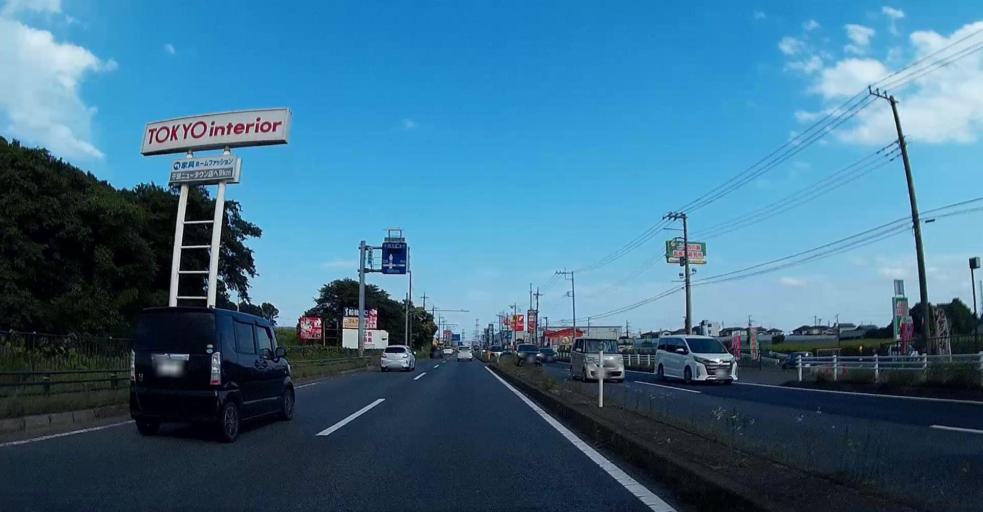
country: JP
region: Chiba
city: Shiroi
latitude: 35.7995
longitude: 140.0551
